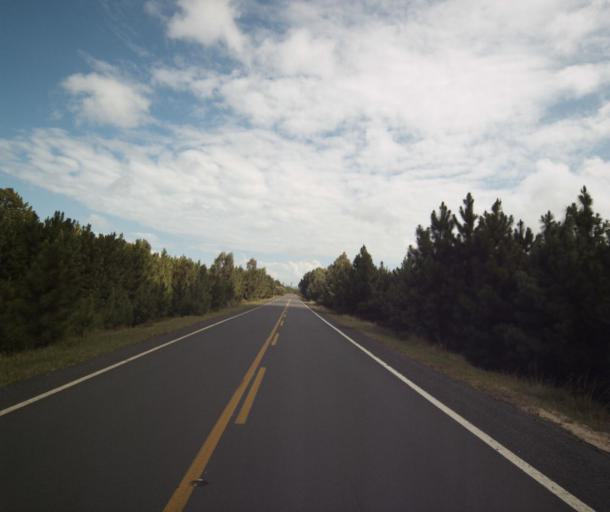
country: BR
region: Rio Grande do Sul
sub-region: Sao Lourenco Do Sul
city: Sao Lourenco do Sul
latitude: -31.4662
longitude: -51.2331
